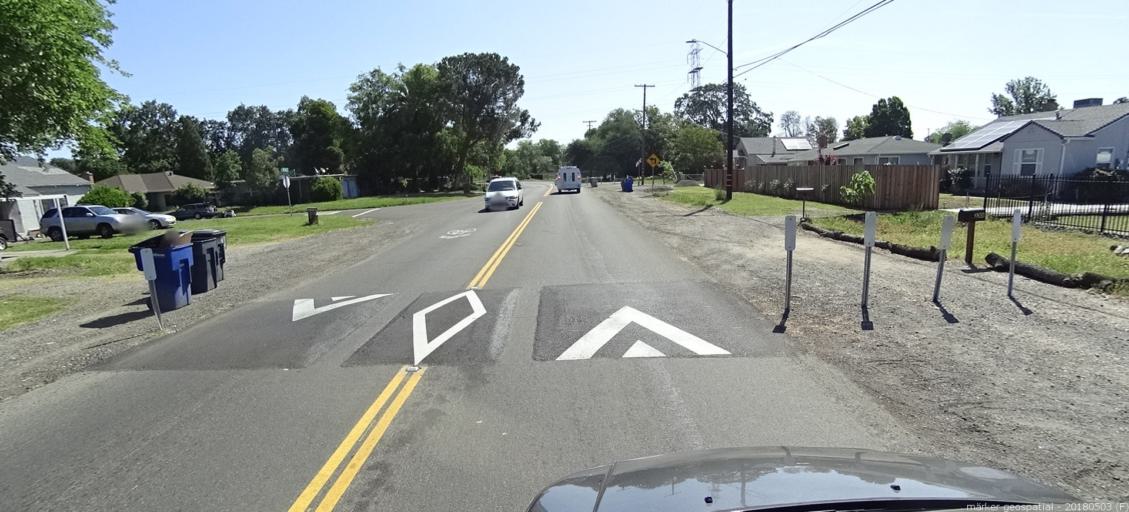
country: US
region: California
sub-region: Sacramento County
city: Arden-Arcade
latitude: 38.6269
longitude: -121.4226
